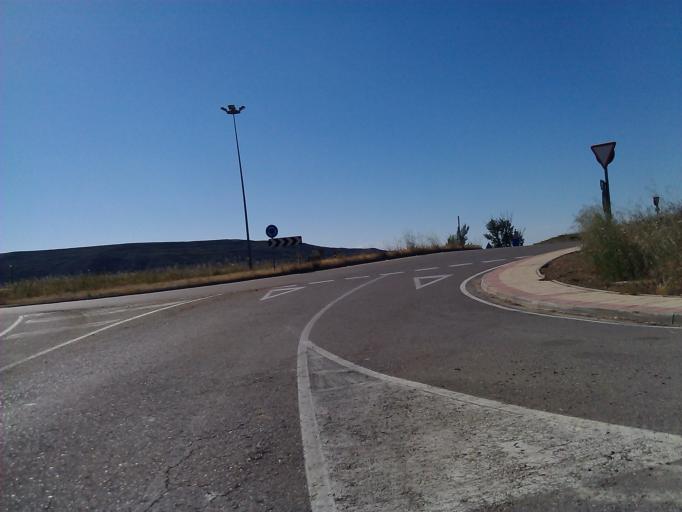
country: ES
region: Castille and Leon
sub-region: Provincia de Burgos
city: Villaquiran de la Puebla
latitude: 42.2885
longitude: -4.1463
